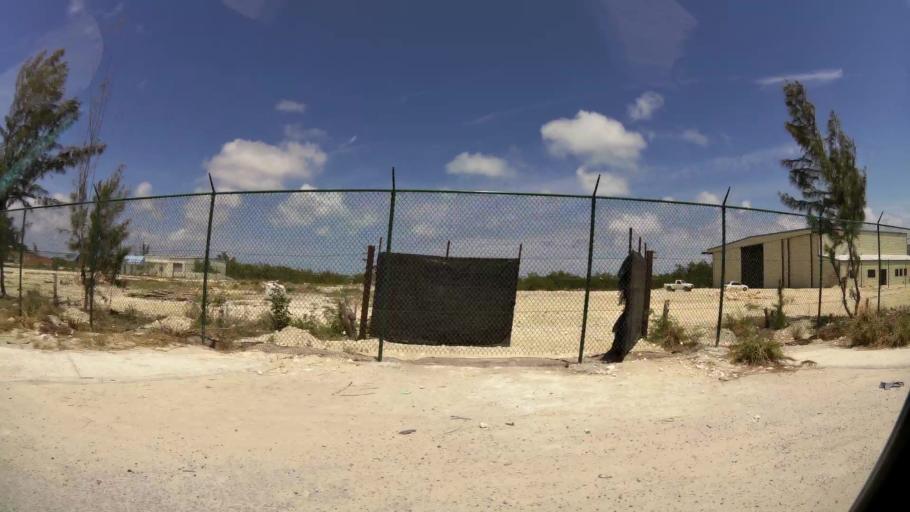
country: BS
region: Mayaguana
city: Abraham's Bay
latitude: 21.7710
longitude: -72.2570
